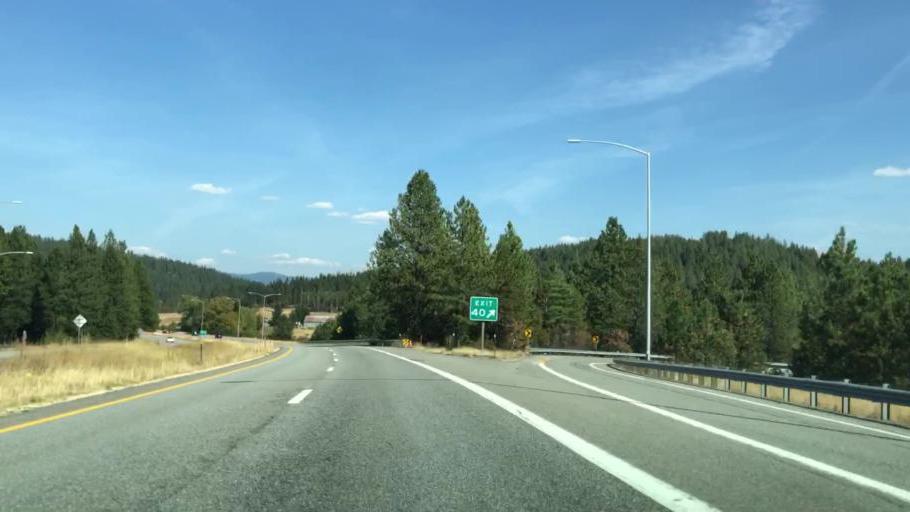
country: US
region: Idaho
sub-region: Shoshone County
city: Pinehurst
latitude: 47.5469
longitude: -116.3288
